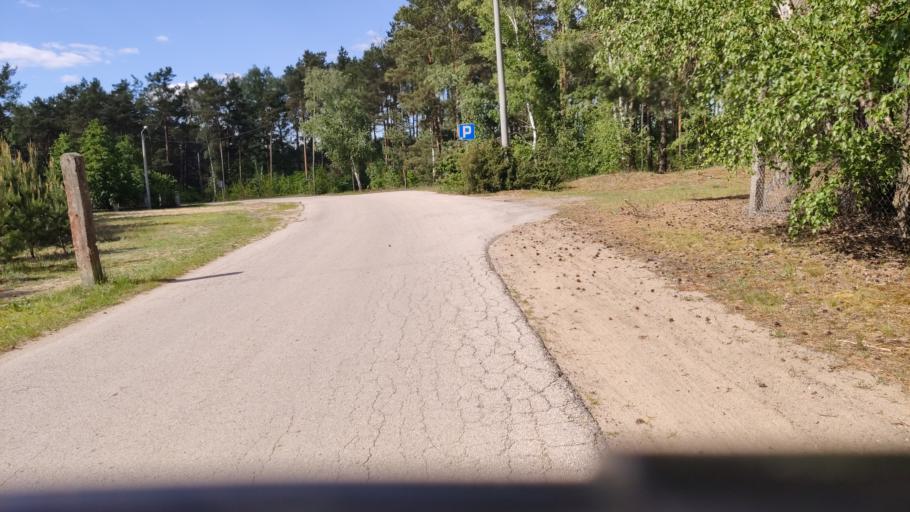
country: PL
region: Kujawsko-Pomorskie
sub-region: Wloclawek
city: Wloclawek
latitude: 52.5952
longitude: 19.0872
